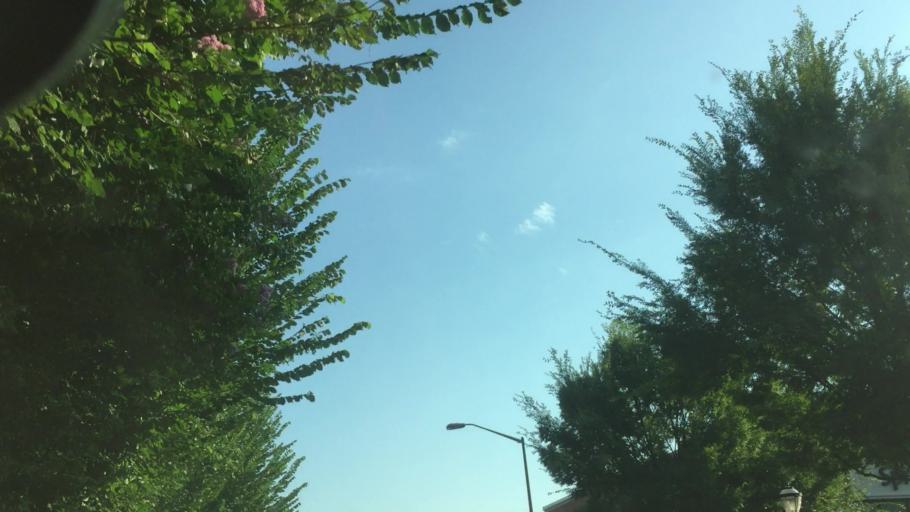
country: US
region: Georgia
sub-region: DeKalb County
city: Druid Hills
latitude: 33.7563
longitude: -84.3491
